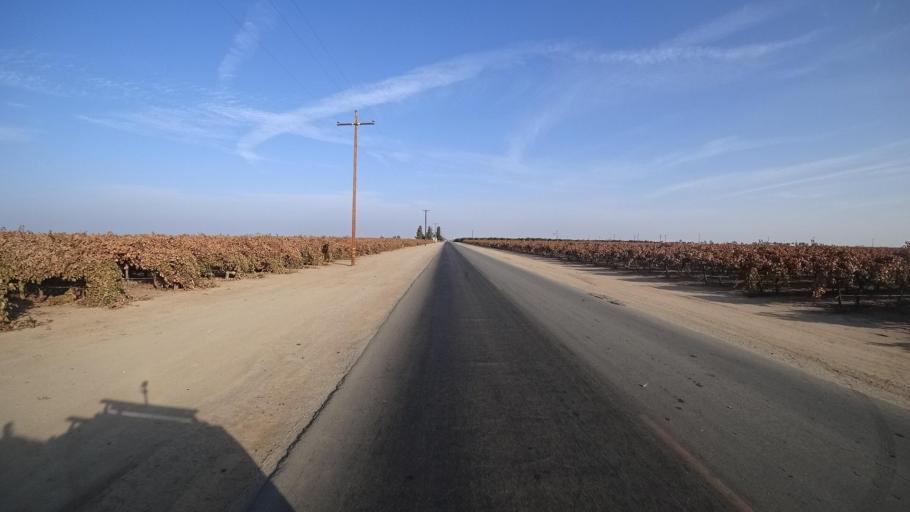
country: US
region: California
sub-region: Kern County
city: Delano
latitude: 35.7552
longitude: -119.1874
